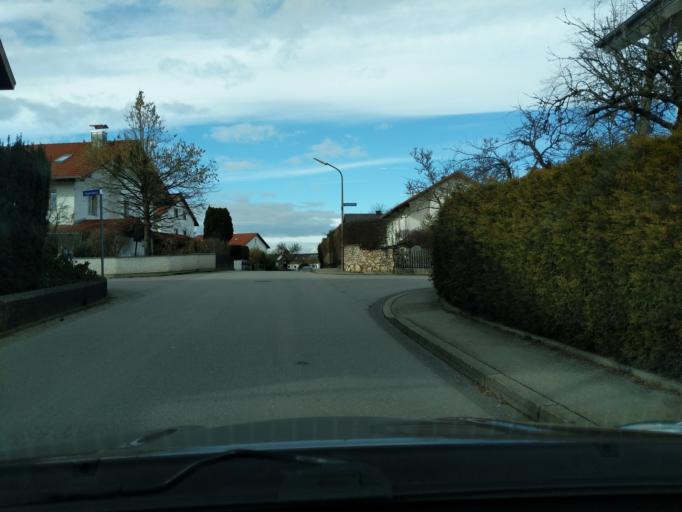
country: DE
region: Bavaria
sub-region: Upper Bavaria
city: Grafing bei Munchen
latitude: 48.0492
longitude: 11.9602
